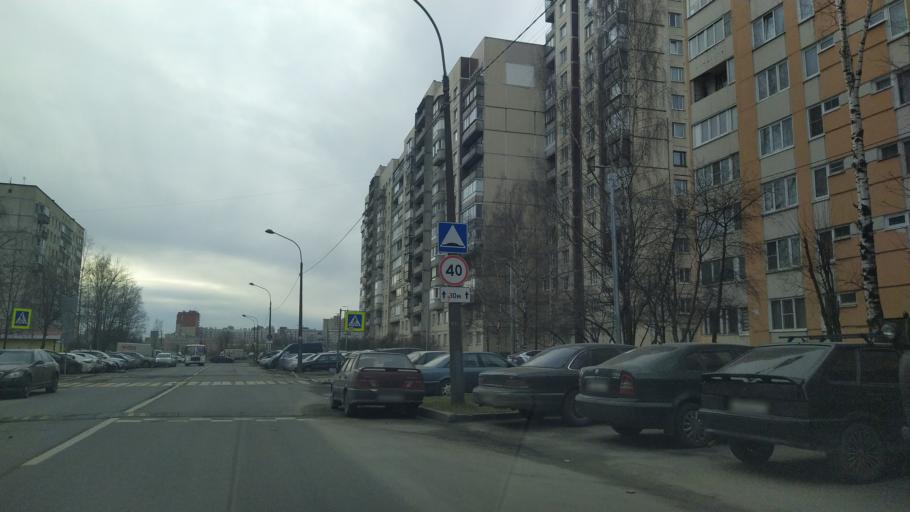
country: RU
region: St.-Petersburg
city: Grazhdanka
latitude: 60.0248
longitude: 30.4211
